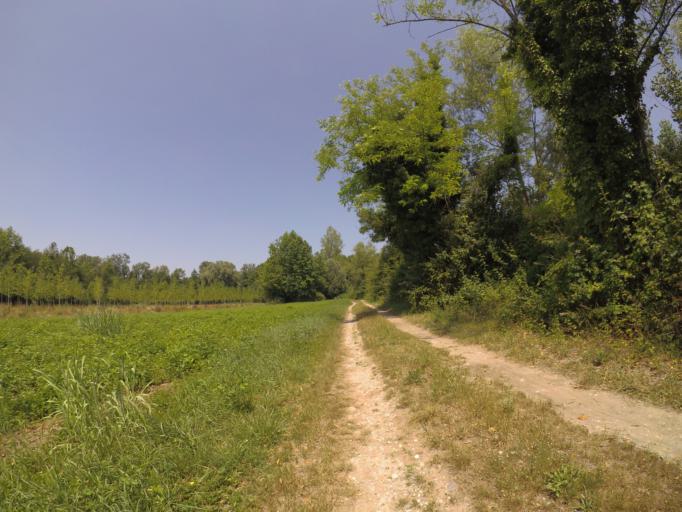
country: IT
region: Friuli Venezia Giulia
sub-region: Provincia di Udine
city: Rivignano
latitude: 45.9032
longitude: 13.0301
